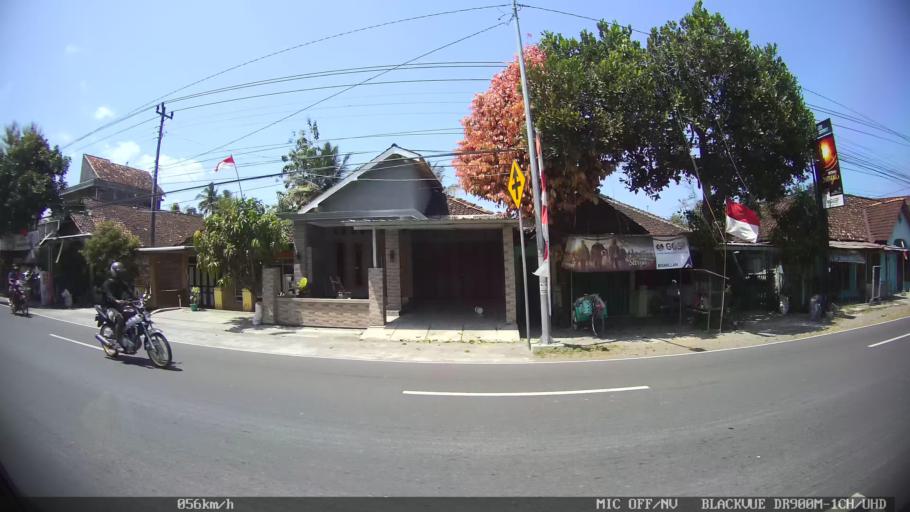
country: ID
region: Daerah Istimewa Yogyakarta
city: Srandakan
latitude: -7.9353
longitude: 110.2606
